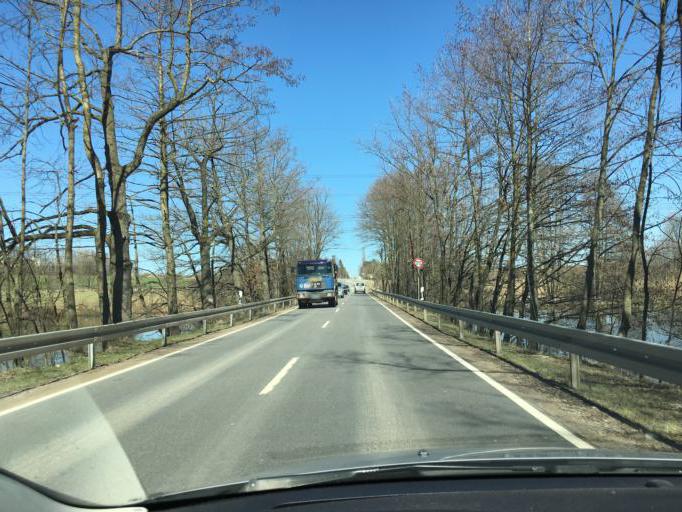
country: DE
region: Saxony
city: Limbach-Oberfrohna
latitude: 50.8737
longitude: 12.7796
